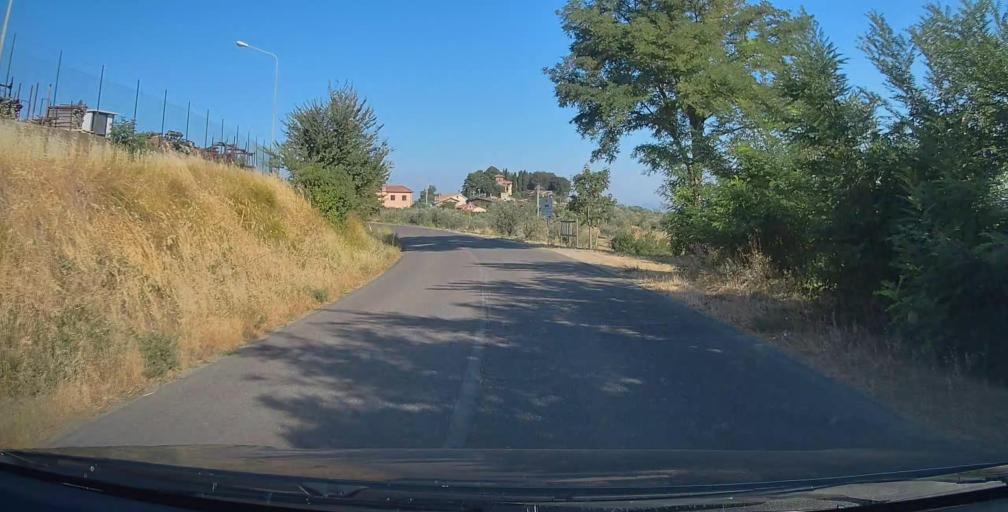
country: IT
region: Umbria
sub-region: Provincia di Terni
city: Calvi dell'Umbria
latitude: 42.4118
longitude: 12.5563
